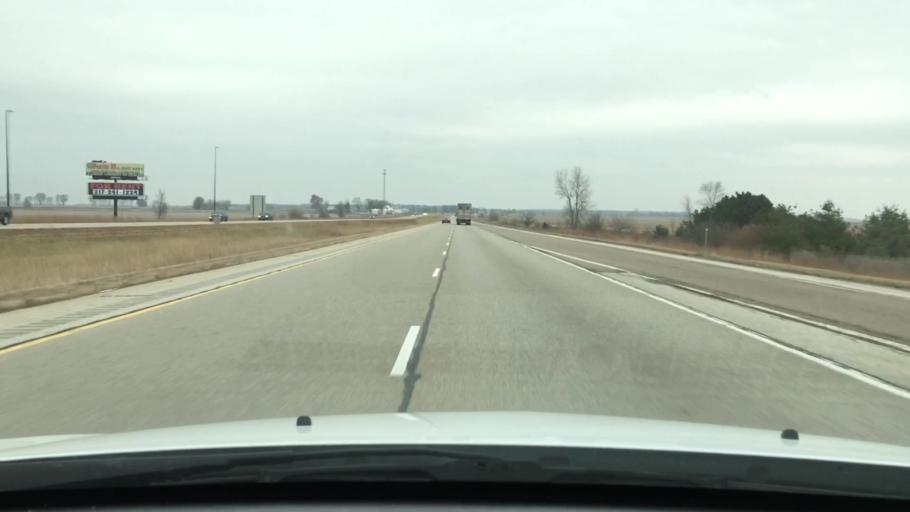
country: US
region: Illinois
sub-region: Logan County
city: Atlanta
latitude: 40.3151
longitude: -89.1603
